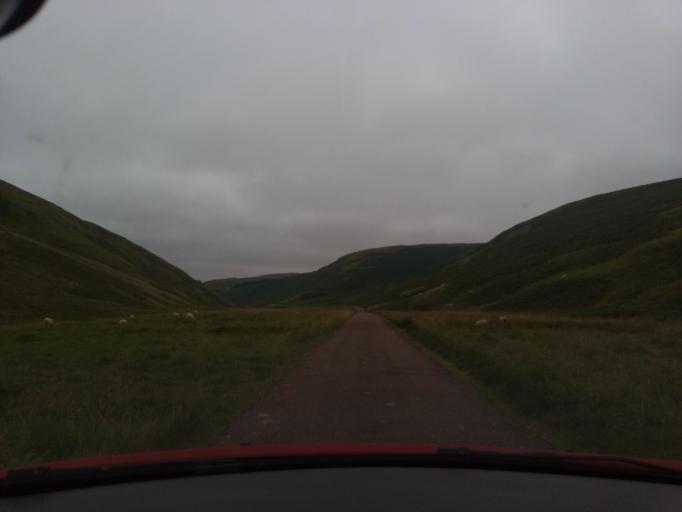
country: GB
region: England
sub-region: Northumberland
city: Rochester
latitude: 55.3840
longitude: -2.2132
